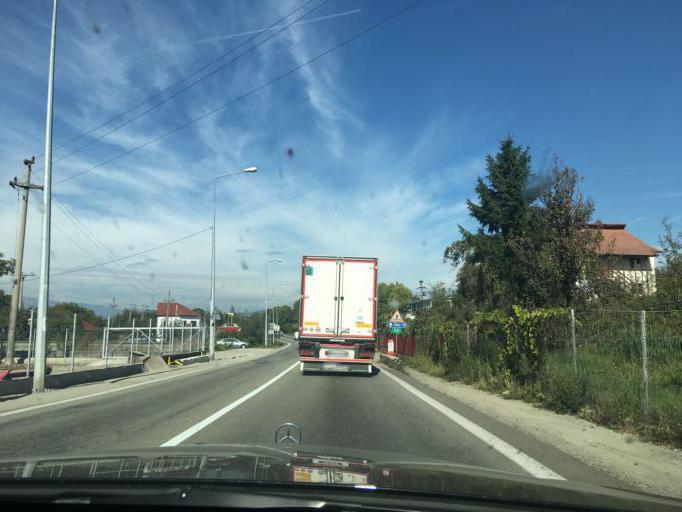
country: RO
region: Valcea
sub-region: Municipiul Ramnicu Valcea
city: Goranu
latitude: 45.1062
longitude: 24.3862
